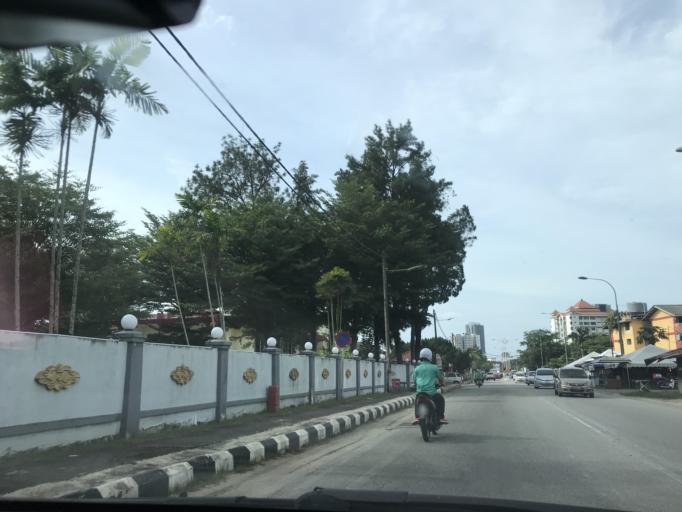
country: MY
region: Kelantan
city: Kota Bharu
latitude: 6.1076
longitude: 102.2365
